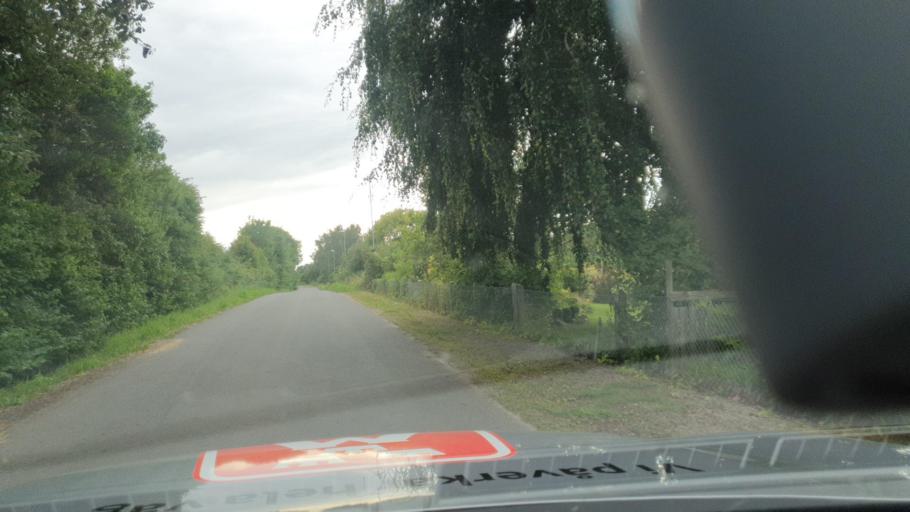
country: SE
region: Skane
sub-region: Bromolla Kommun
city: Bromoella
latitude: 56.1013
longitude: 14.4999
